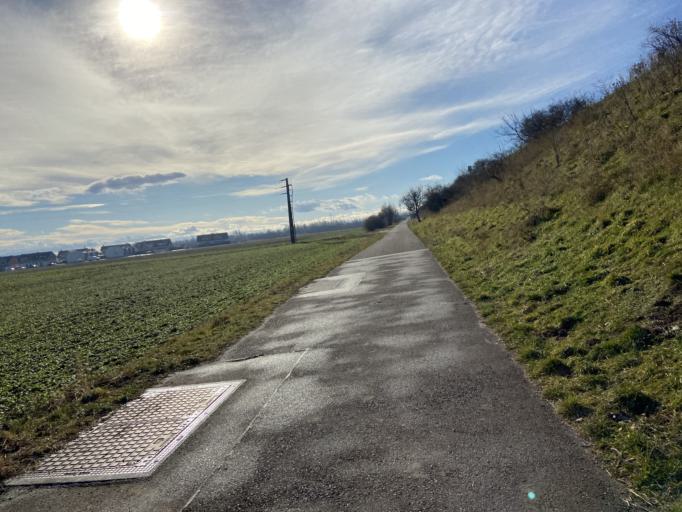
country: AT
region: Lower Austria
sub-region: Politischer Bezirk Modling
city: Laxenburg
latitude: 48.0681
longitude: 16.3450
